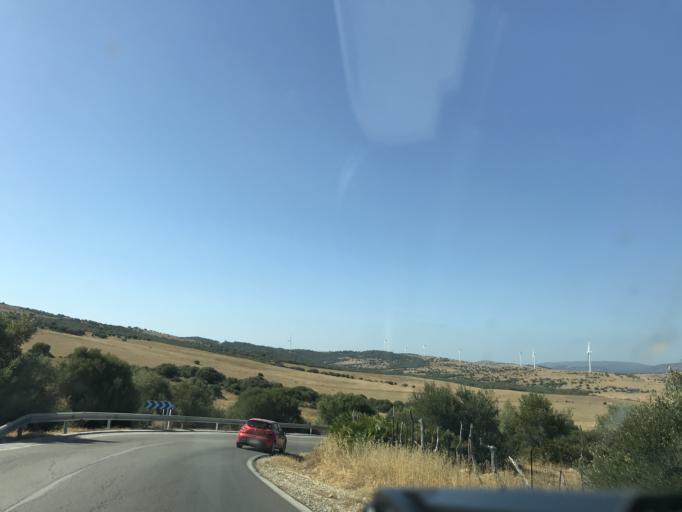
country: ES
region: Andalusia
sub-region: Provincia de Cadiz
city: Zahara de los Atunes
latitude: 36.1033
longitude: -5.7202
